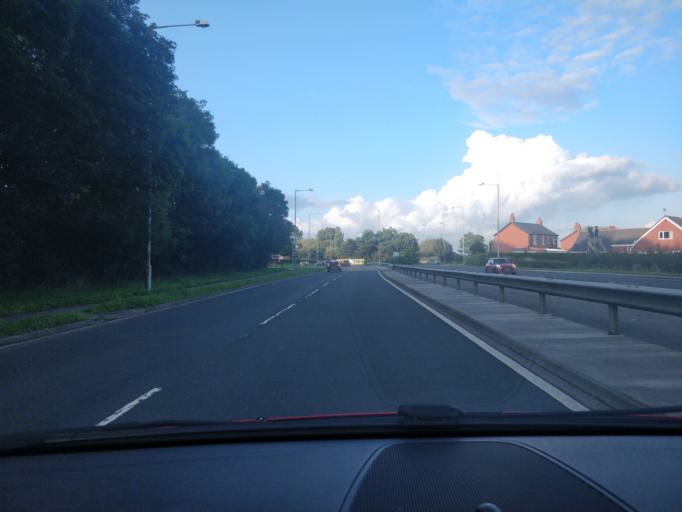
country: GB
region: England
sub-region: Lancashire
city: Croston
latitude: 53.7120
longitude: -2.7802
